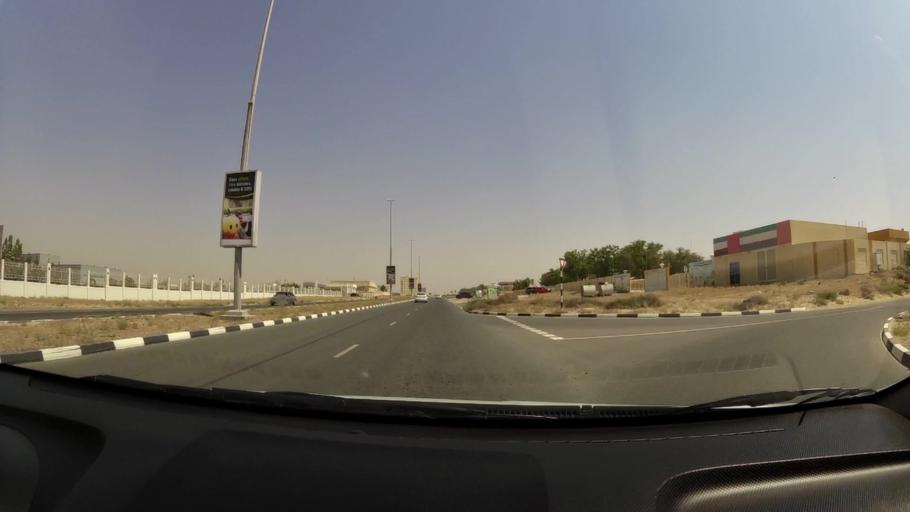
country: AE
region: Umm al Qaywayn
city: Umm al Qaywayn
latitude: 25.5020
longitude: 55.5962
